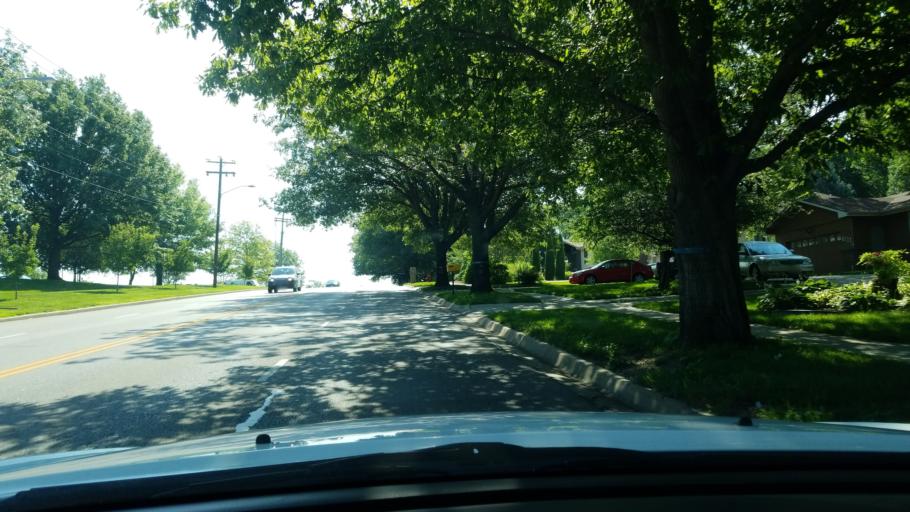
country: US
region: Nebraska
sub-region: Lancaster County
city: Lincoln
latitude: 40.7989
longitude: -96.6299
